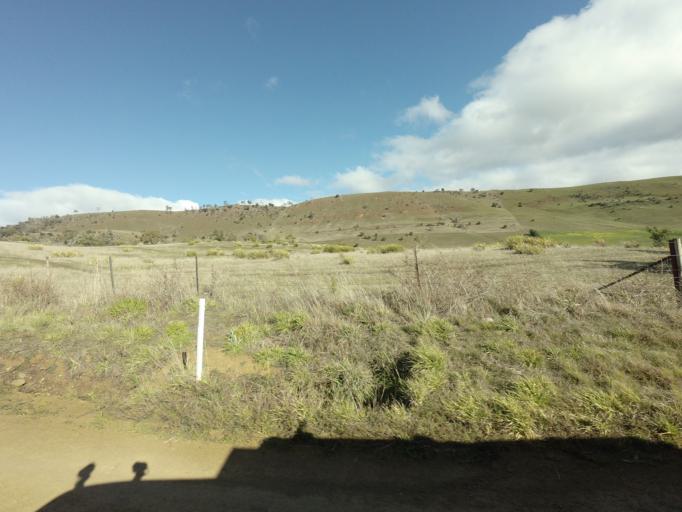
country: AU
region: Tasmania
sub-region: Derwent Valley
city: New Norfolk
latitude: -42.7032
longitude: 146.9928
